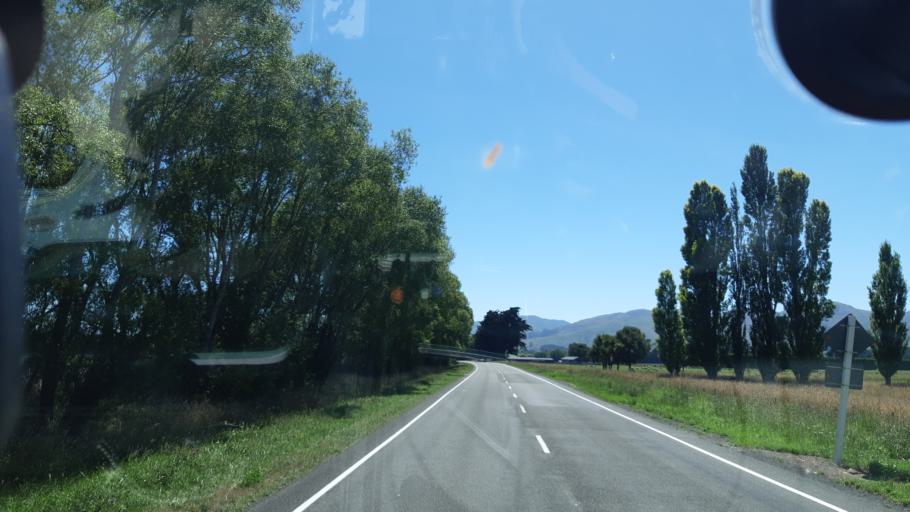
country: NZ
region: Canterbury
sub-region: Kaikoura District
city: Kaikoura
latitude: -42.7371
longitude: 173.2692
